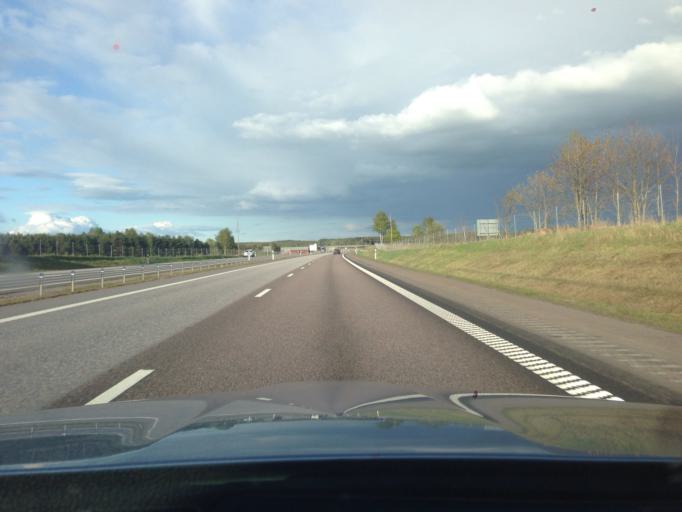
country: SE
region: OEstergoetland
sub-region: Mjolby Kommun
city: Mantorp
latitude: 58.3741
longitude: 15.3132
